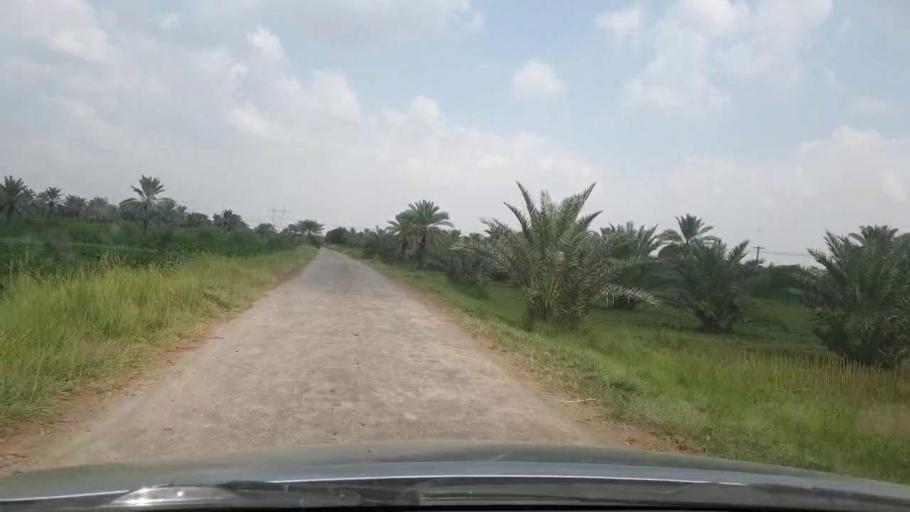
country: PK
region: Sindh
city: Khairpur
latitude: 27.4656
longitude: 68.7607
